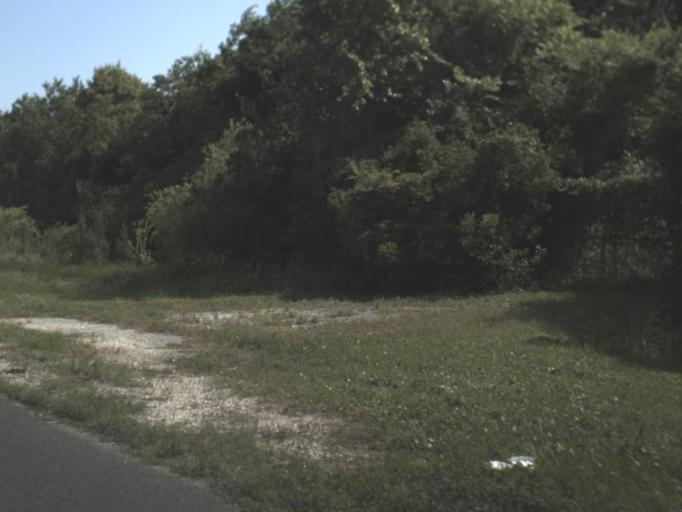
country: US
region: Florida
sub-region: Saint Johns County
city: Villano Beach
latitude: 29.9310
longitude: -81.3295
